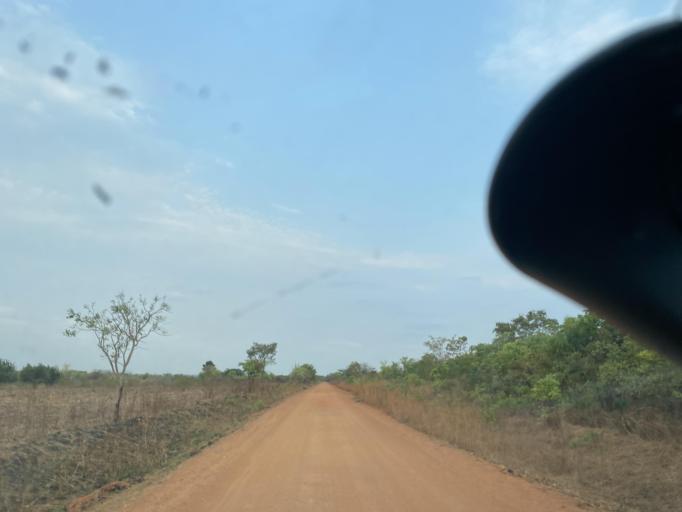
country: ZM
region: Lusaka
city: Chongwe
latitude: -15.2216
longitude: 28.5860
